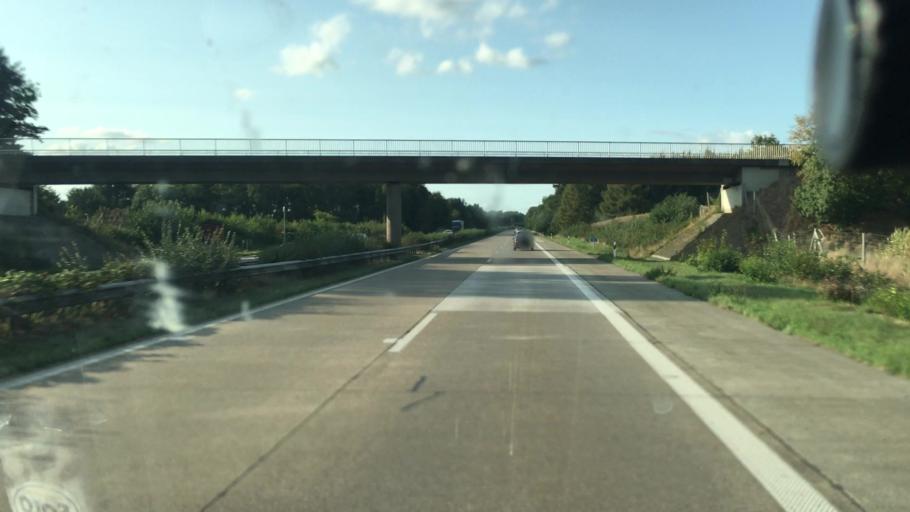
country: DE
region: Lower Saxony
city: Rastede
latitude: 53.2602
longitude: 8.1685
